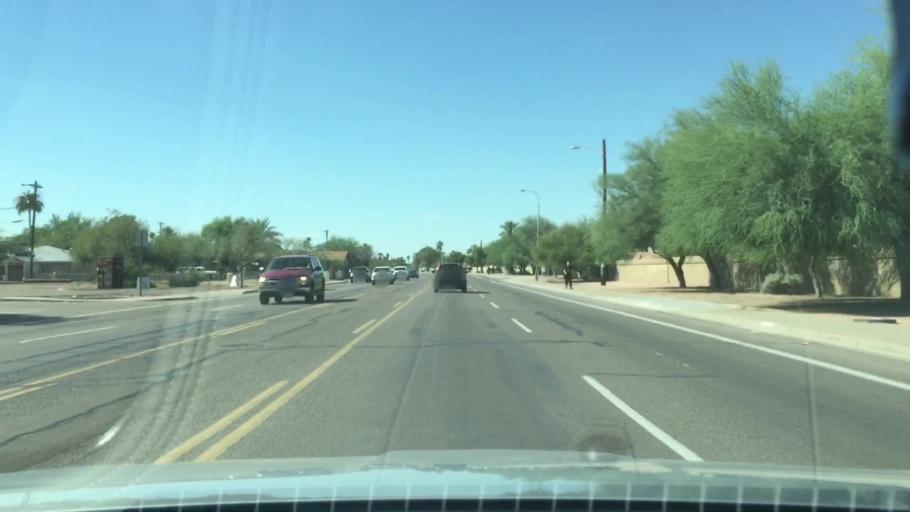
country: US
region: Arizona
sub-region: Maricopa County
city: Phoenix
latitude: 33.3927
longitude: -112.0498
